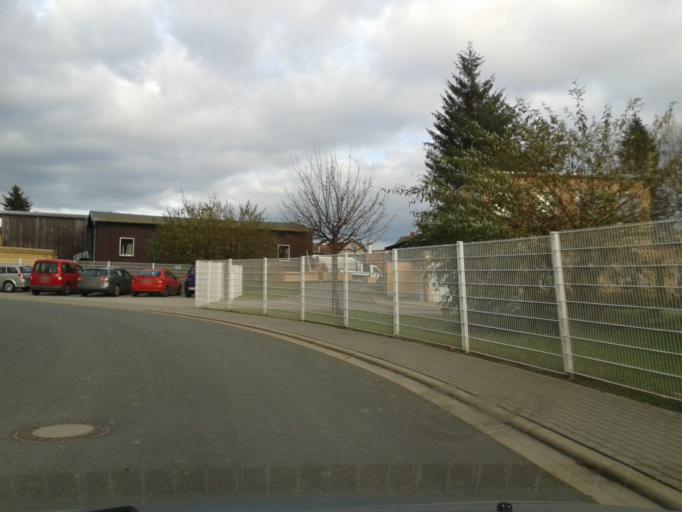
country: DE
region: Thuringia
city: Hermsdorf
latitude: 50.8978
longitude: 11.8531
